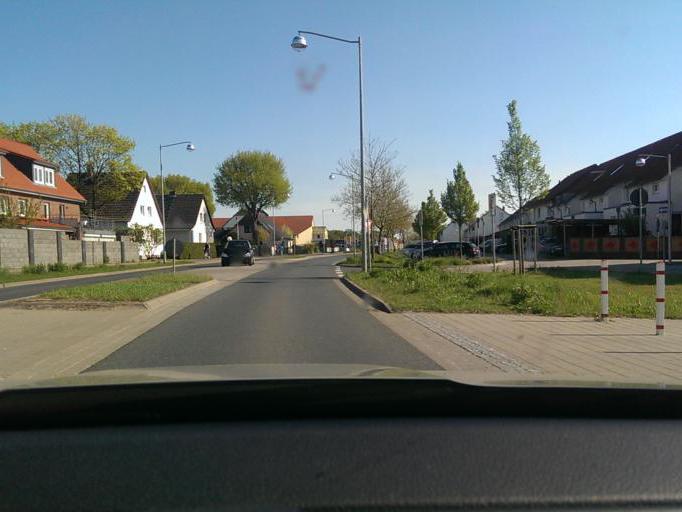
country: DE
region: Lower Saxony
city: Langenhagen
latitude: 52.4825
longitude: 9.7330
